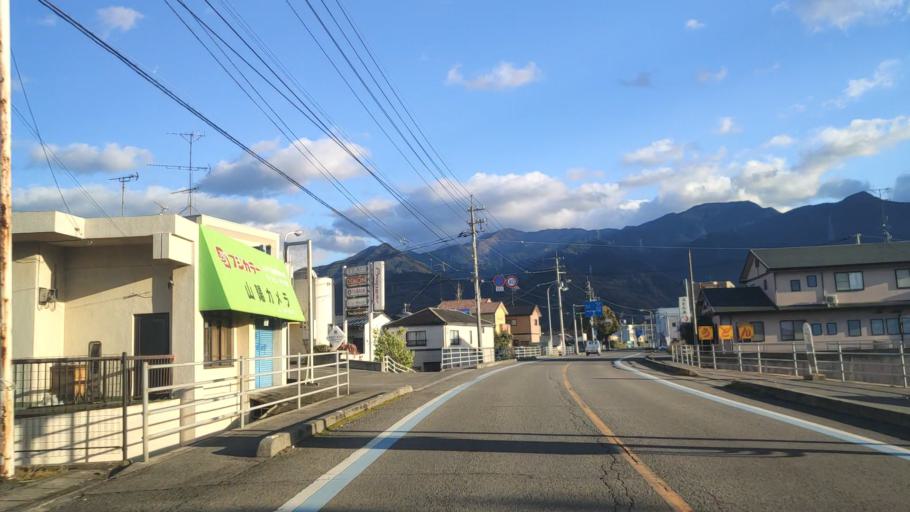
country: JP
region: Ehime
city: Saijo
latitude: 33.9084
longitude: 133.1838
